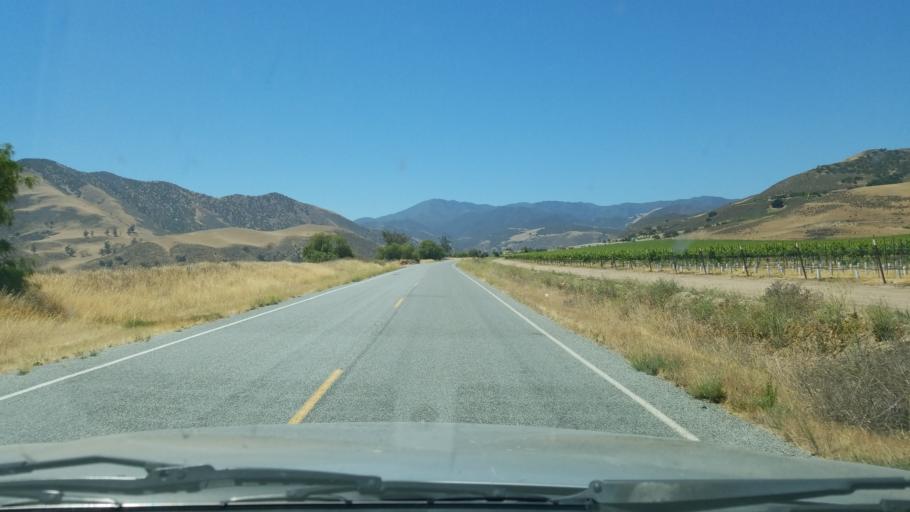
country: US
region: California
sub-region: Monterey County
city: Greenfield
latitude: 36.2946
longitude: -121.3148
